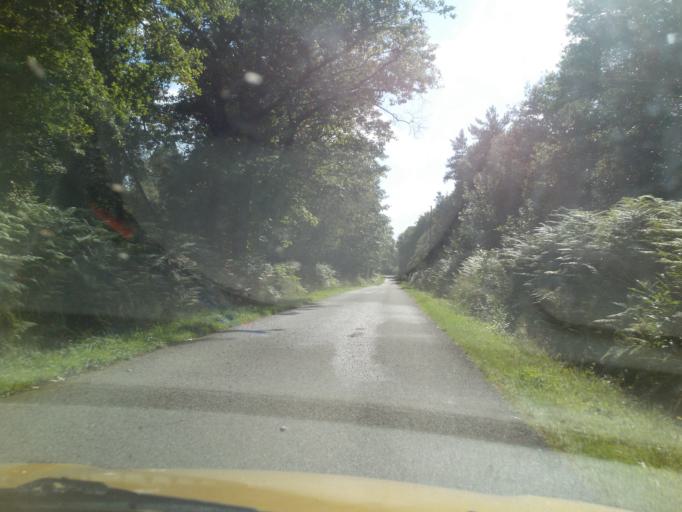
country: FR
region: Brittany
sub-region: Departement des Cotes-d'Armor
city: Merdrignac
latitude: 48.1259
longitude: -2.3880
